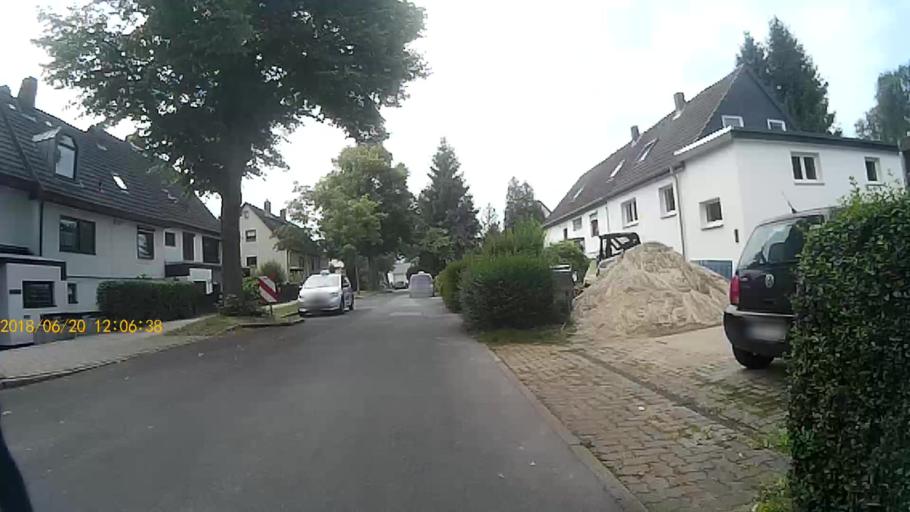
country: DE
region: Hamburg
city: Harburg
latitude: 53.4896
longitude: 10.0095
